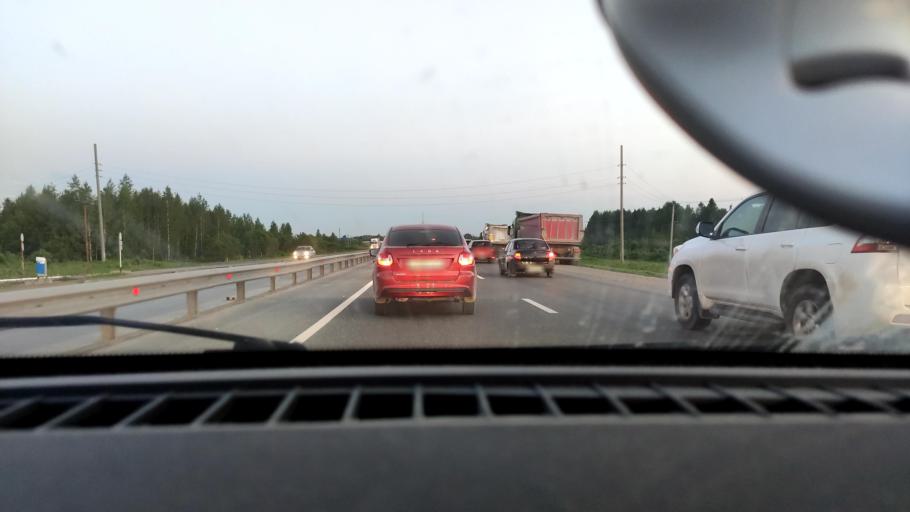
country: RU
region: Perm
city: Polazna
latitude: 58.2102
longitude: 56.4048
